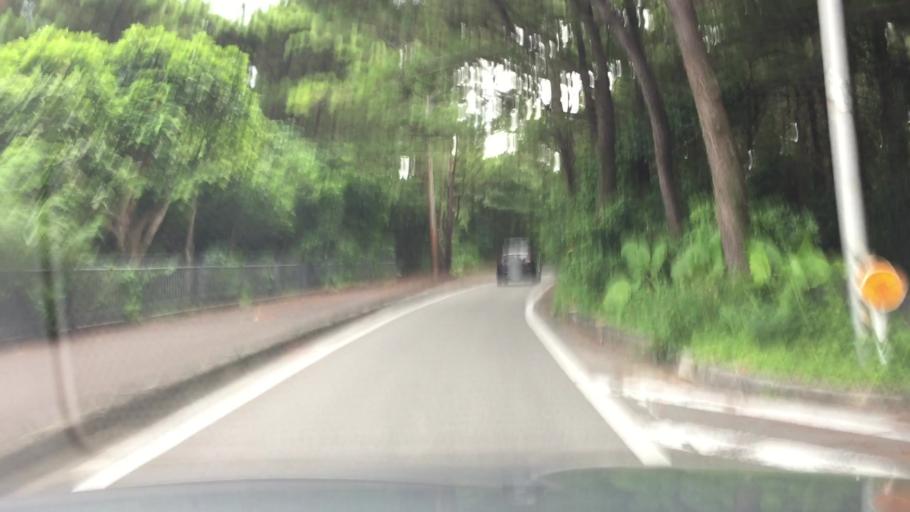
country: JP
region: Okinawa
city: Ishigaki
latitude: 24.4479
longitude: 124.1287
